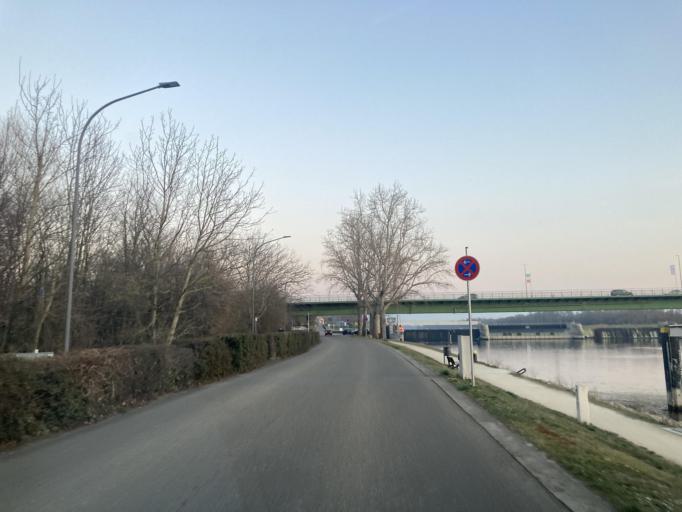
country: DE
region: Baden-Wuerttemberg
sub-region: Freiburg Region
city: Breisach am Rhein
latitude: 48.0241
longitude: 7.5817
